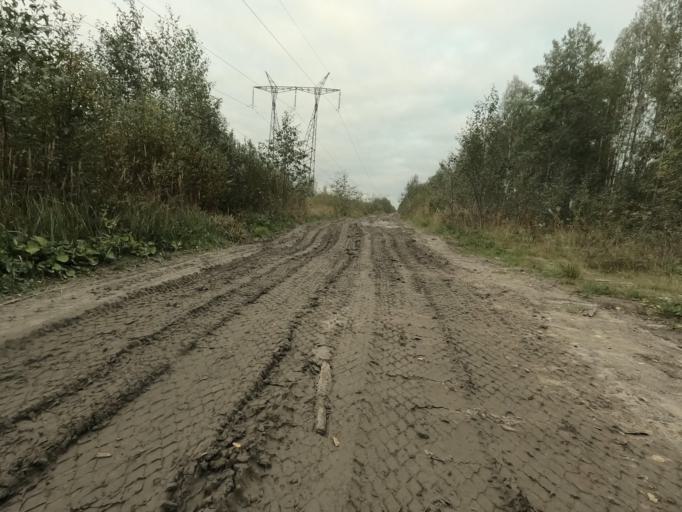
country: RU
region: St.-Petersburg
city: Sapernyy
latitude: 59.7545
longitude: 30.6945
